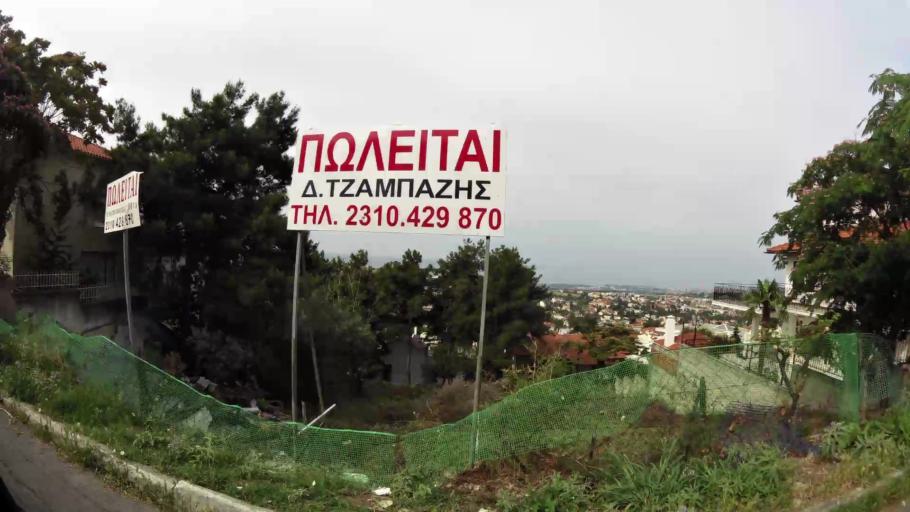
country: GR
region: Central Macedonia
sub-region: Nomos Thessalonikis
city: Panorama
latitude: 40.5855
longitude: 23.0286
